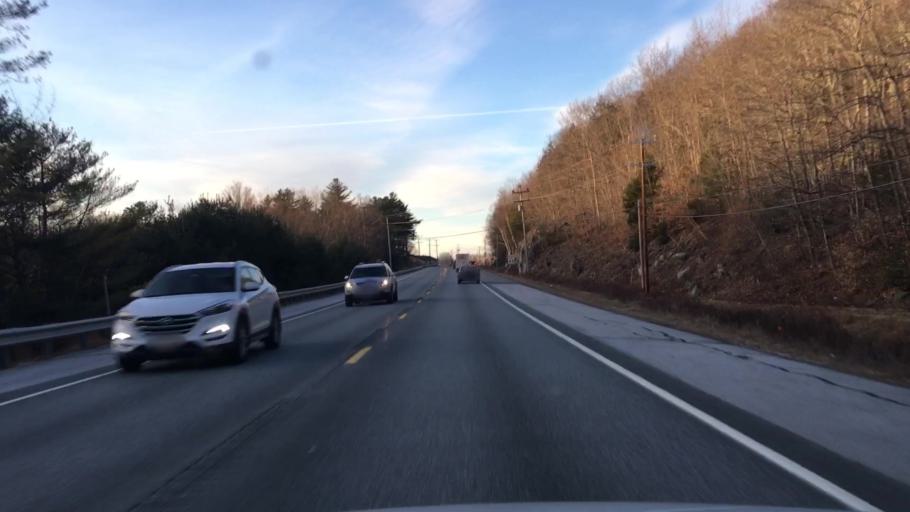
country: US
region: Maine
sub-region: Hancock County
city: Dedham
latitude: 44.7241
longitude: -68.6191
